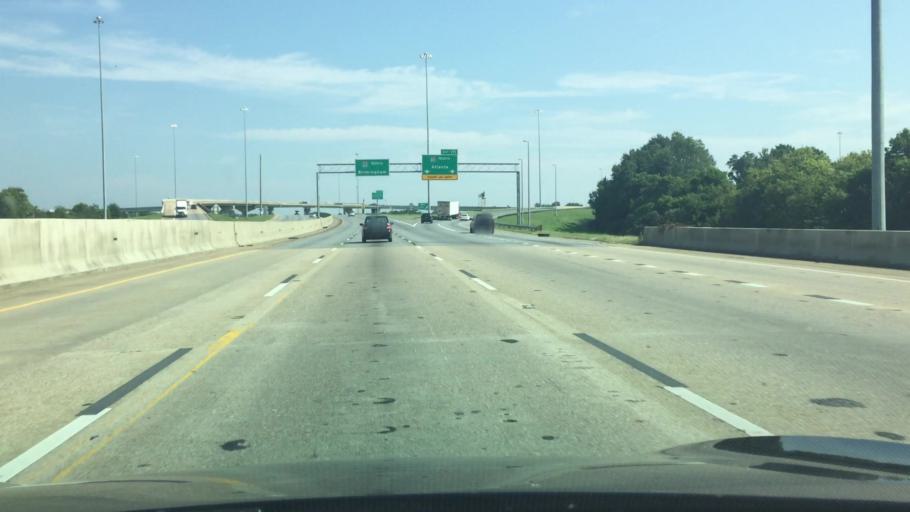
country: US
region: Alabama
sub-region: Montgomery County
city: Montgomery
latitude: 32.3624
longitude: -86.3217
